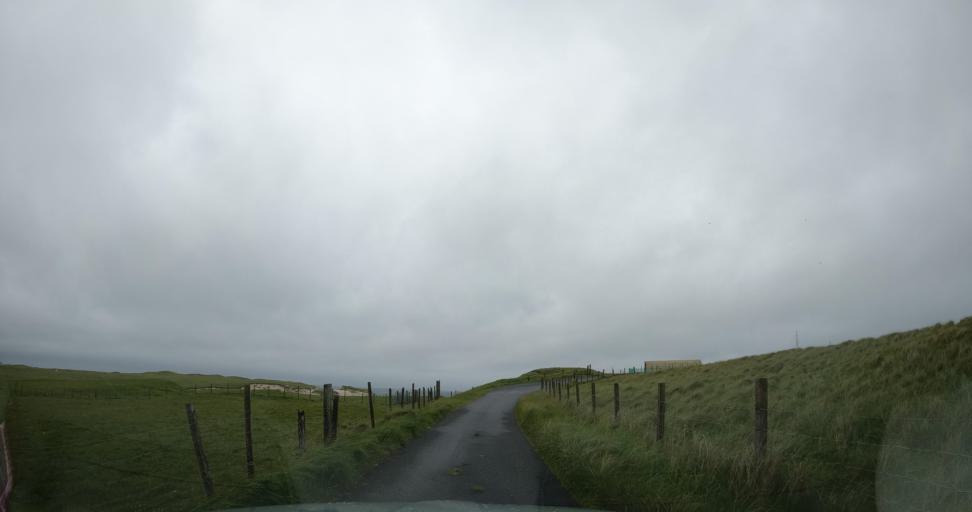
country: GB
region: Scotland
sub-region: Eilean Siar
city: Barra
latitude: 57.0053
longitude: -7.4991
